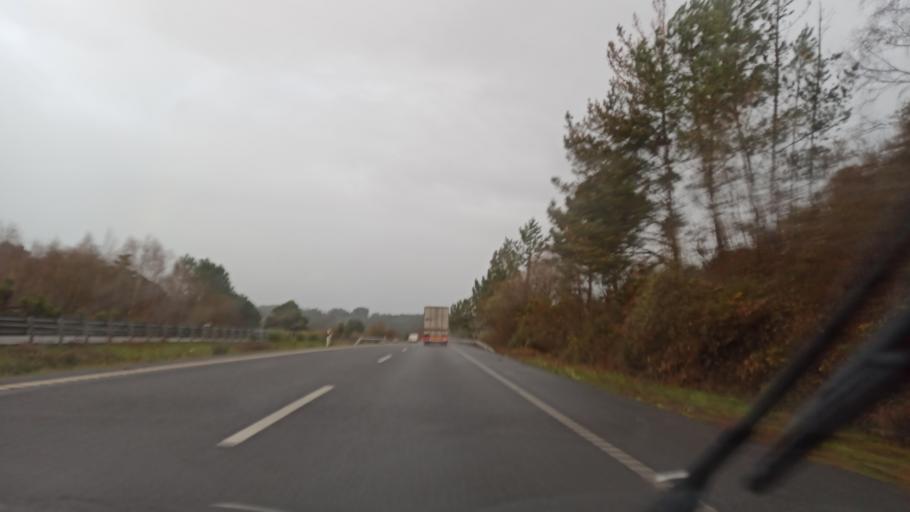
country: ES
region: Galicia
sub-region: Provincia da Coruna
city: Cambre
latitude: 43.2667
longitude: -8.3032
